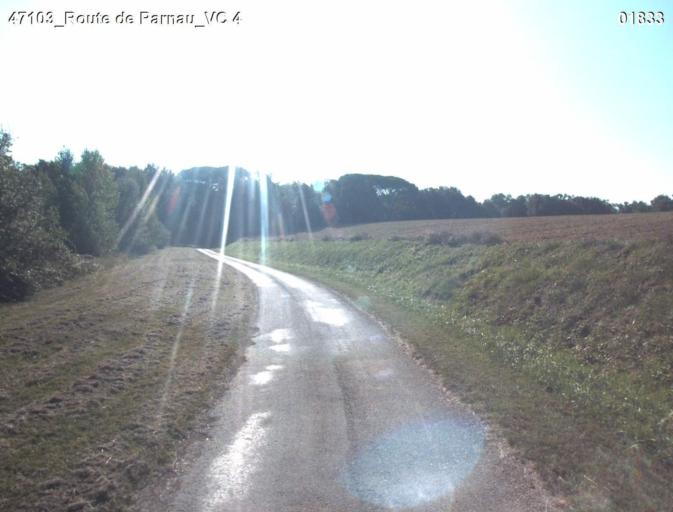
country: FR
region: Aquitaine
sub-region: Departement du Lot-et-Garonne
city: Nerac
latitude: 44.0791
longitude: 0.3504
